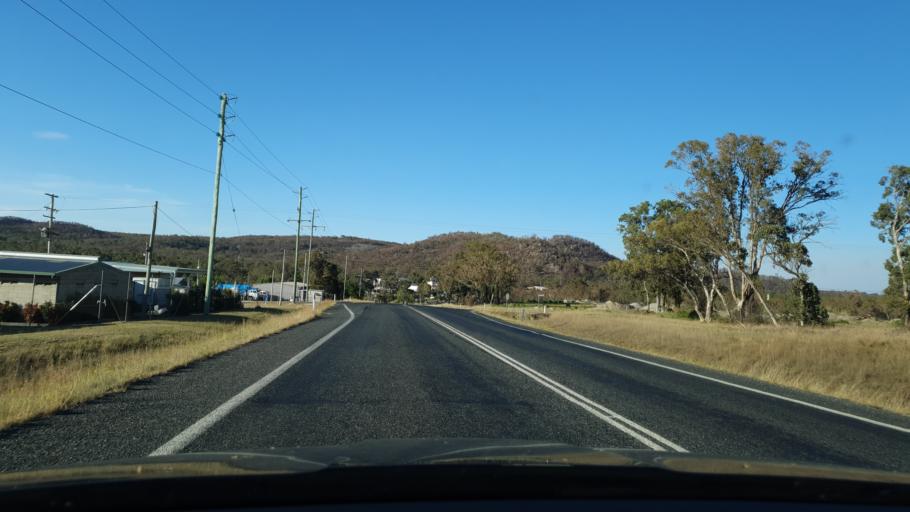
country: AU
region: Queensland
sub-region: Southern Downs
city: Stanthorpe
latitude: -28.6574
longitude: 151.9171
